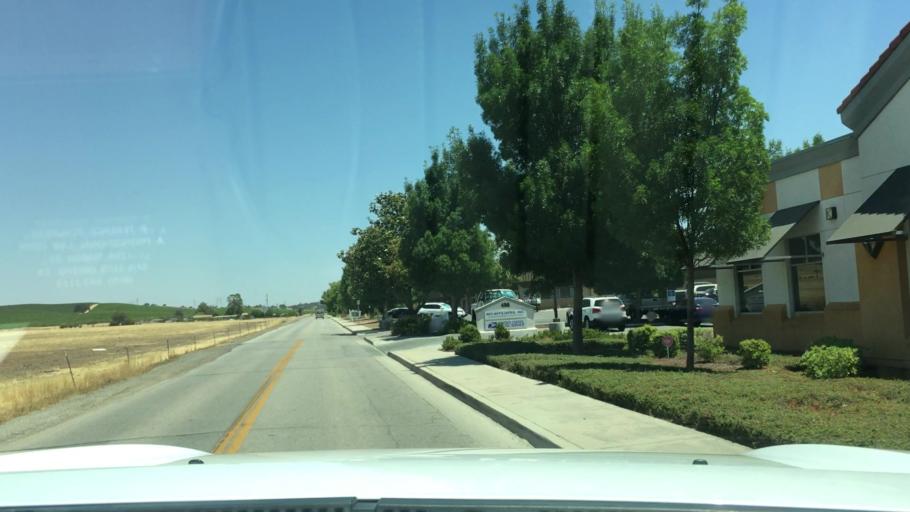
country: US
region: California
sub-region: San Luis Obispo County
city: Paso Robles
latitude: 35.6132
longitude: -120.6499
